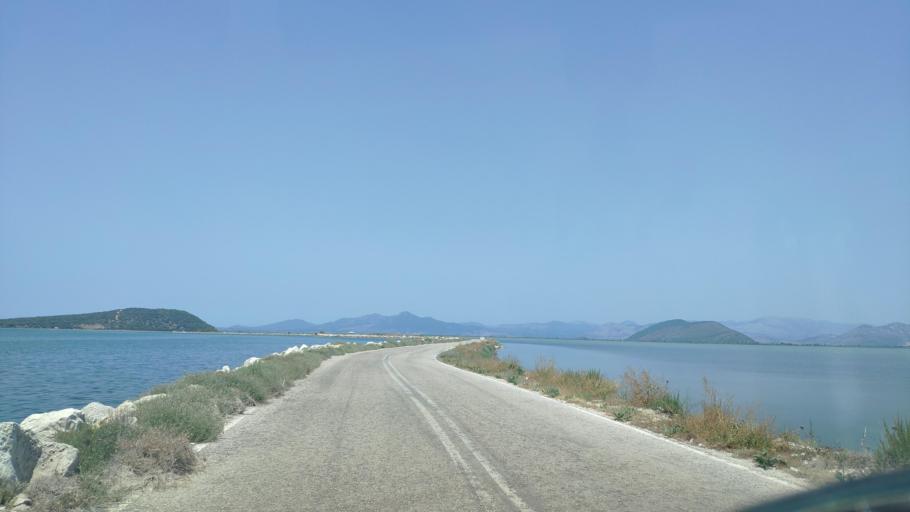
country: GR
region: Epirus
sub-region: Nomos Artas
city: Aneza
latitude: 39.0295
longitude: 20.9003
